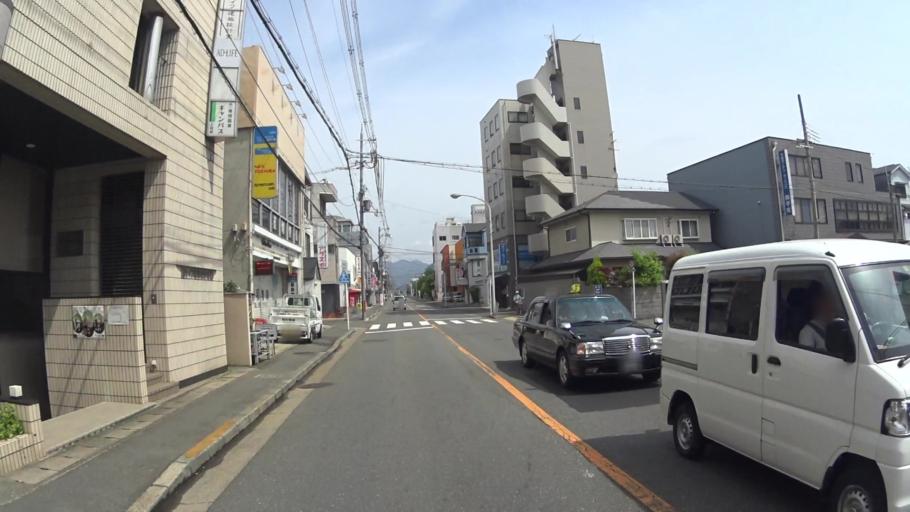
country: JP
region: Kyoto
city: Muko
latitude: 34.9860
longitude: 135.6930
